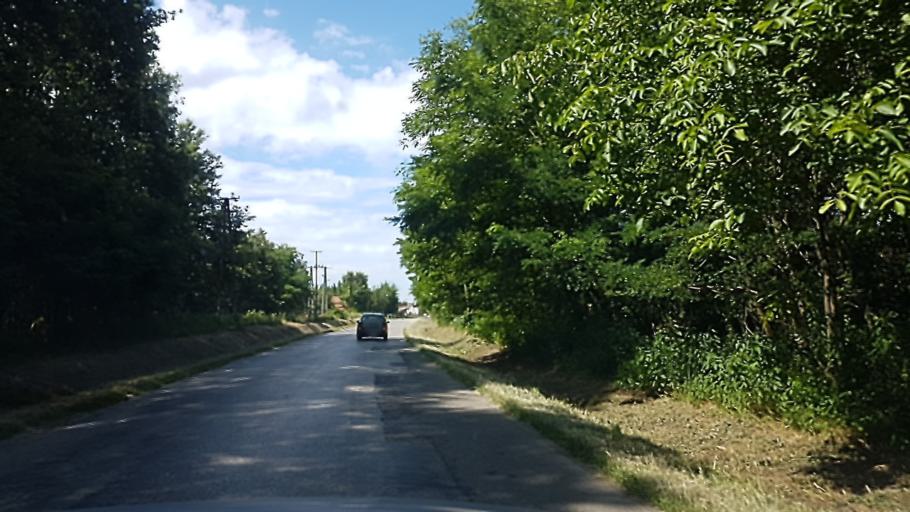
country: HU
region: Somogy
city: Barcs
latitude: 45.9681
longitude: 17.5891
